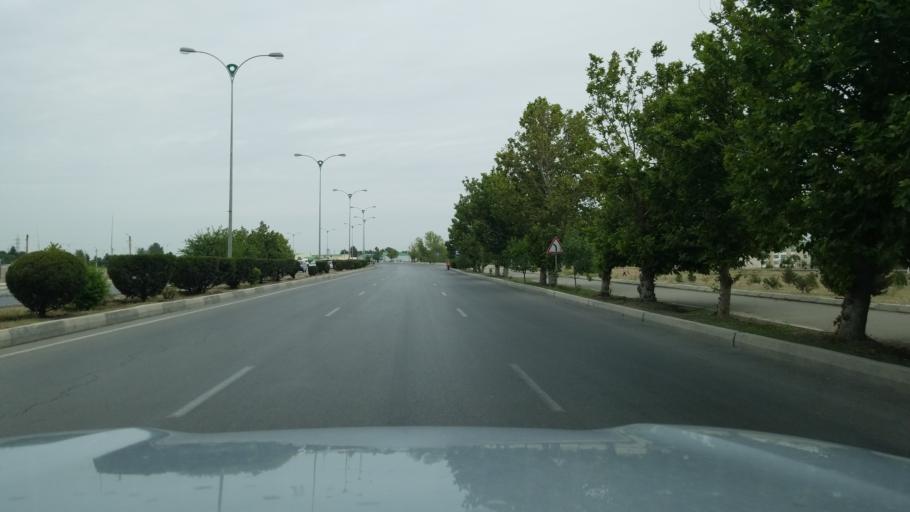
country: TM
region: Ahal
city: Abadan
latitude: 38.0539
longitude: 58.1832
